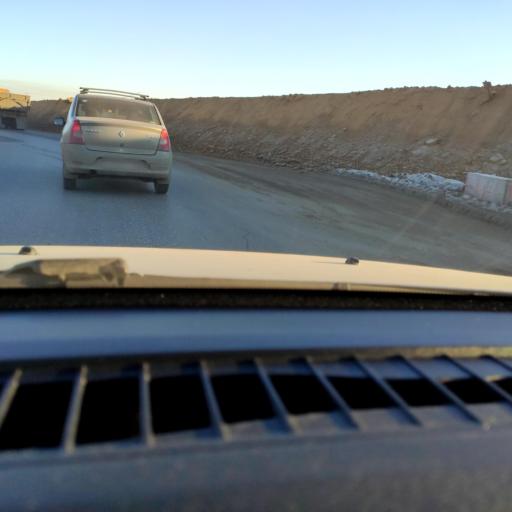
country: RU
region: Samara
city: Podstepki
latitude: 53.5613
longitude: 49.1990
